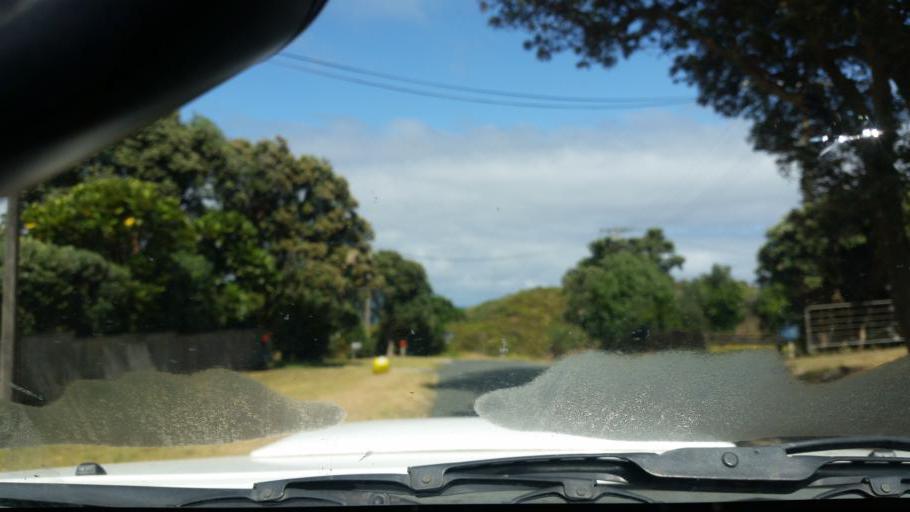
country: NZ
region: Northland
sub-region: Kaipara District
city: Dargaville
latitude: -35.9518
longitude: 173.7462
